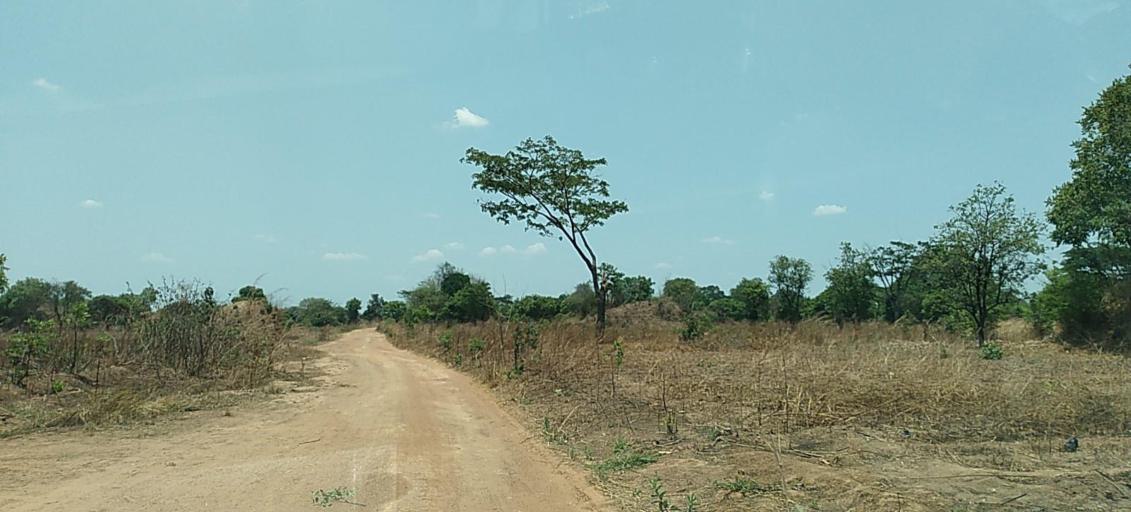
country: ZM
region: Copperbelt
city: Luanshya
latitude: -13.0841
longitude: 28.4056
